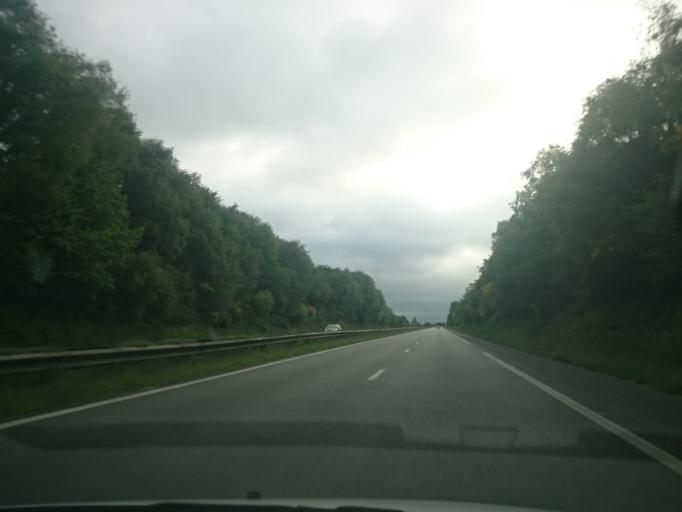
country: FR
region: Brittany
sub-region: Departement du Finistere
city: Saint-Yvi
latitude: 47.9400
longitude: -3.9195
